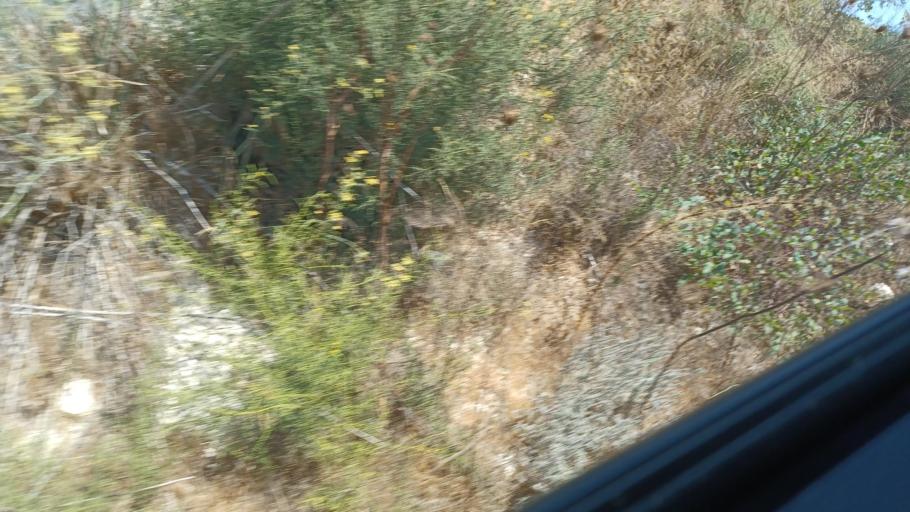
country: CY
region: Pafos
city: Mesogi
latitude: 34.8500
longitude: 32.4696
